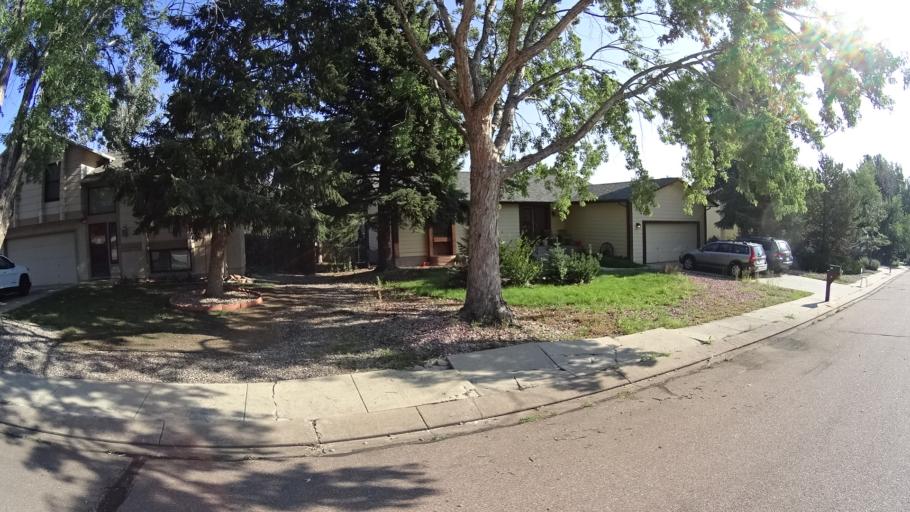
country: US
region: Colorado
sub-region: El Paso County
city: Colorado Springs
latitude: 38.8850
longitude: -104.8459
